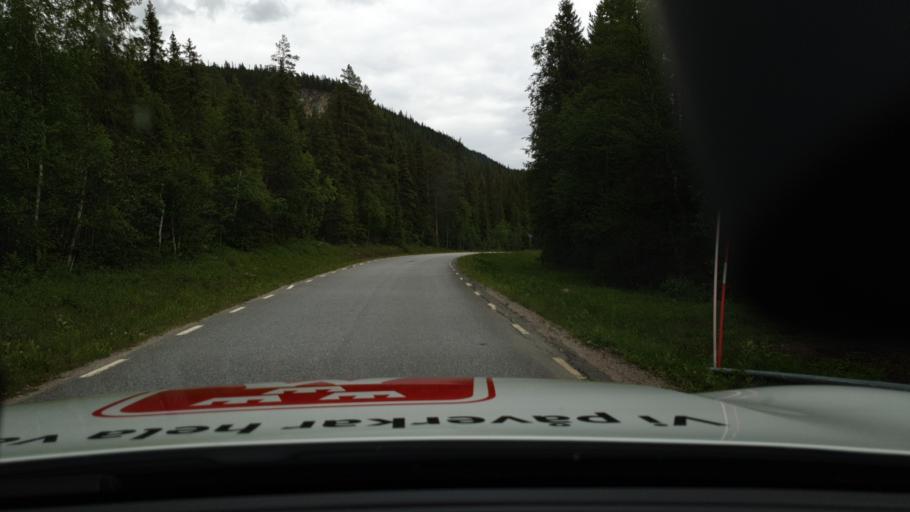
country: SE
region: Norrbotten
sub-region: Arjeplogs Kommun
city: Arjeplog
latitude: 66.8985
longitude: 17.8595
